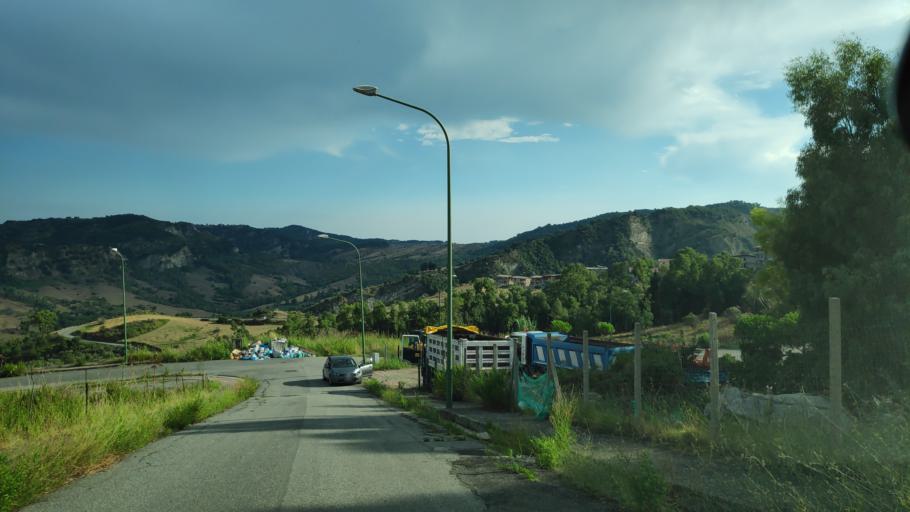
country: IT
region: Calabria
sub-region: Provincia di Reggio Calabria
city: Stilo
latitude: 38.4755
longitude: 16.4686
